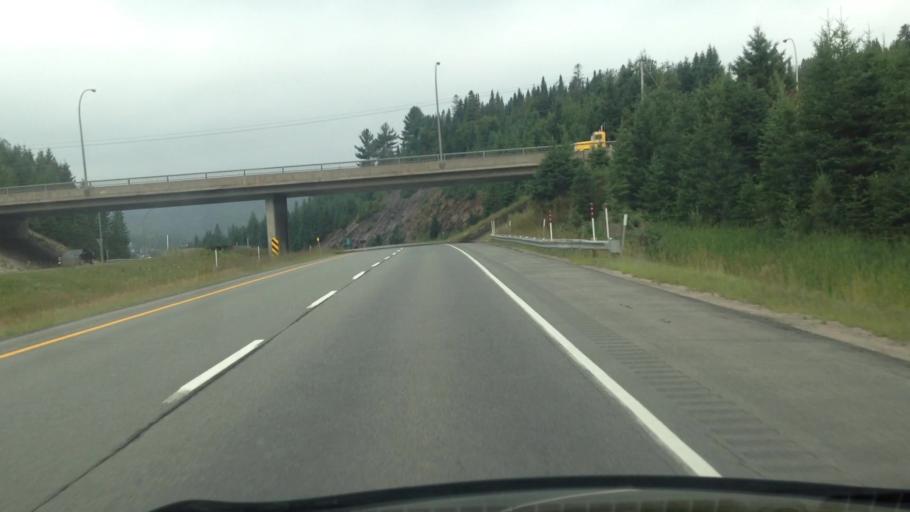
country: CA
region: Quebec
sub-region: Laurentides
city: Sainte-Agathe-des-Monts
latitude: 46.0631
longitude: -74.2875
